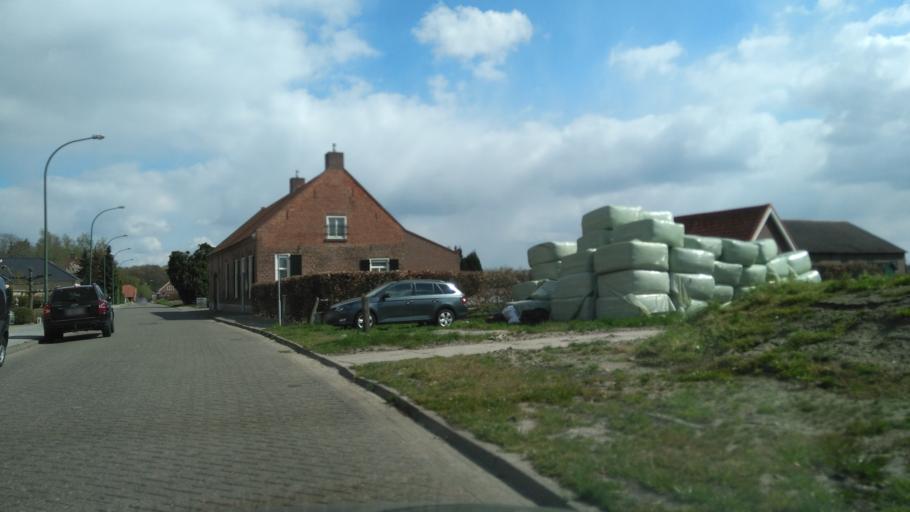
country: NL
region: North Brabant
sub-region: Gemeente Baarle-Nassau
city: Baarle-Nassau
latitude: 51.4419
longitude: 4.9374
